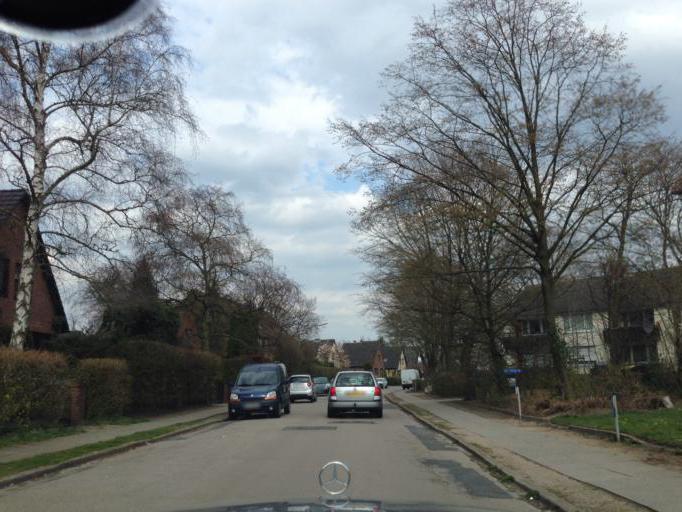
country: DE
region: Hamburg
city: Farmsen-Berne
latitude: 53.5860
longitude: 10.1354
